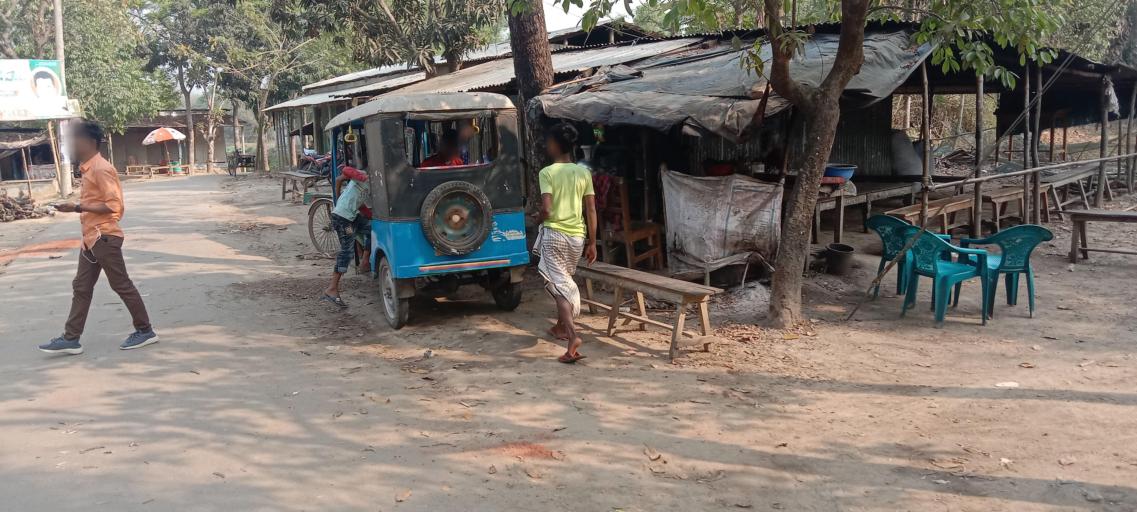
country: BD
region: Dhaka
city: Sakhipur
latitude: 24.4622
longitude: 90.3142
